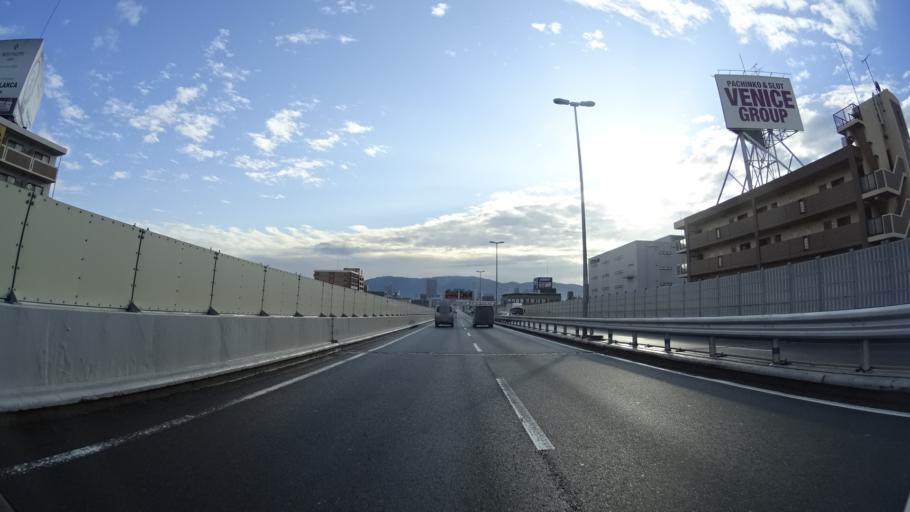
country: JP
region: Osaka
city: Daitocho
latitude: 34.6789
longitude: 135.5827
